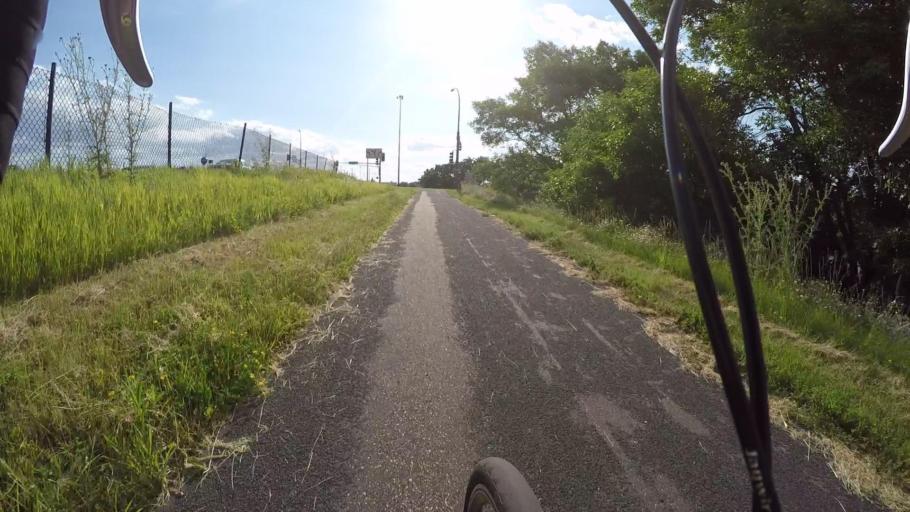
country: US
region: Minnesota
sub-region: Hennepin County
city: Eden Prairie
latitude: 44.8626
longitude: -93.4585
